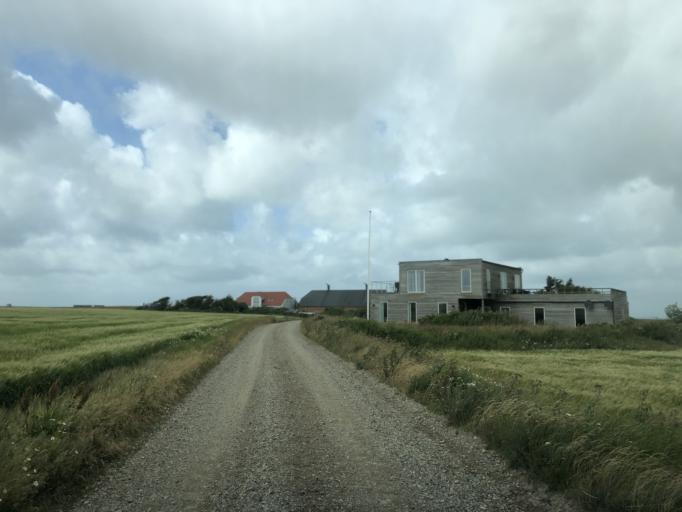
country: DK
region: Central Jutland
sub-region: Lemvig Kommune
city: Harboore
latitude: 56.5127
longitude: 8.1275
